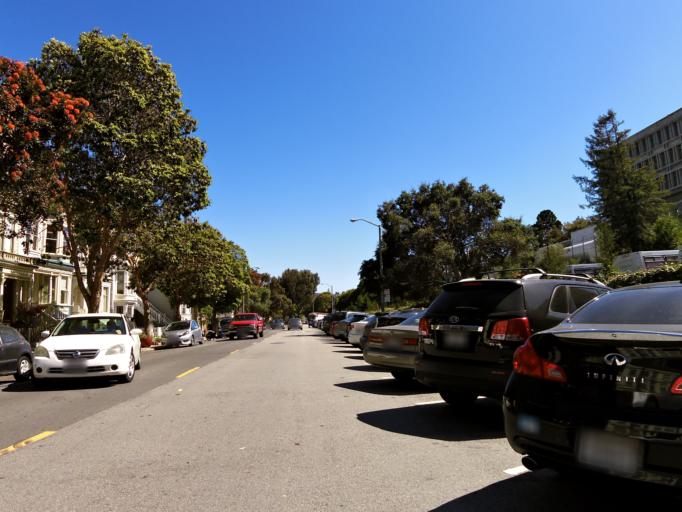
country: US
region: California
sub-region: San Francisco County
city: San Francisco
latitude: 37.7688
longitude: -122.4336
